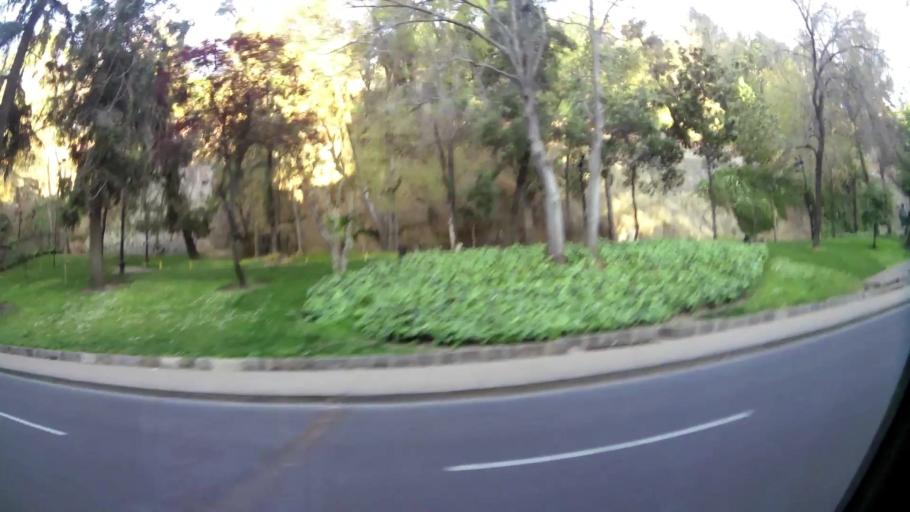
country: CL
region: Santiago Metropolitan
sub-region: Provincia de Santiago
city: Santiago
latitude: -33.4396
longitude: -70.6442
